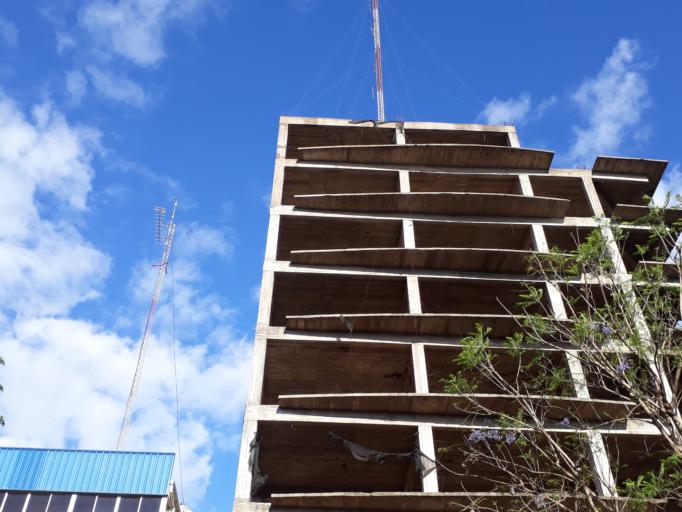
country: AR
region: Misiones
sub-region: Departamento de Capital
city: Posadas
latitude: -27.3721
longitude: -55.9325
